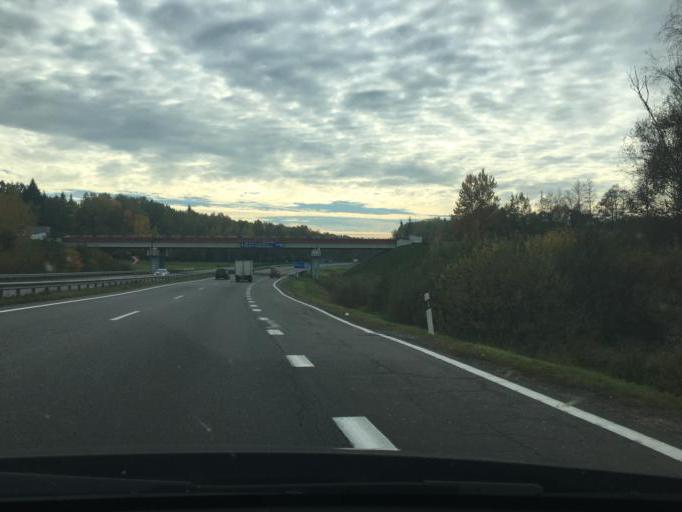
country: BY
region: Minsk
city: Enyerhyetykaw
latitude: 53.5920
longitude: 27.0406
